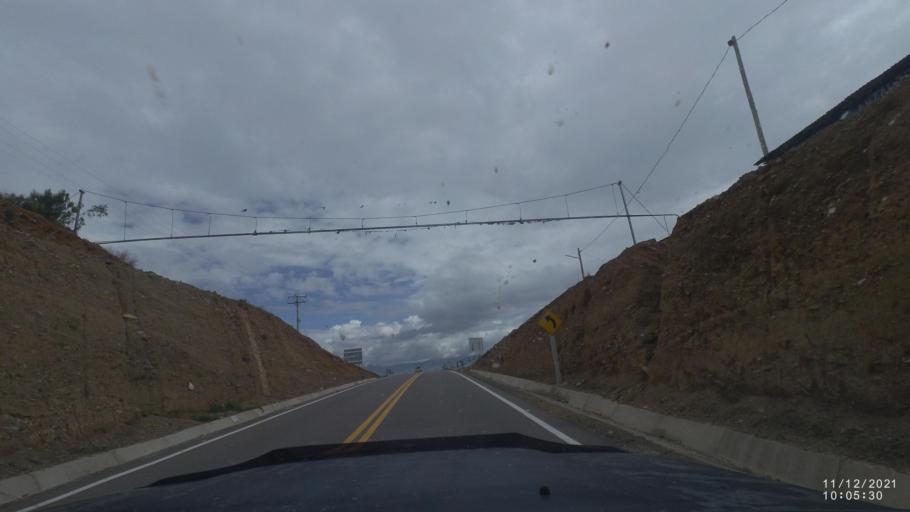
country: BO
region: Cochabamba
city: Cliza
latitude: -17.6991
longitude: -65.9472
